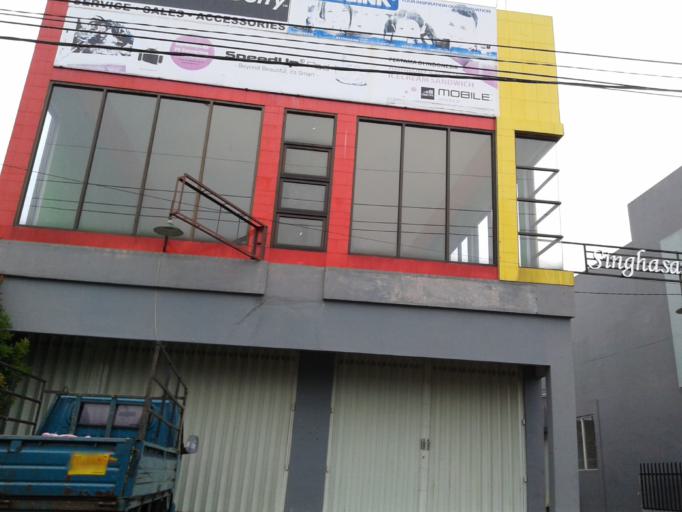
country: ID
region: East Java
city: Singosari
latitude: -7.8960
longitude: 112.6607
